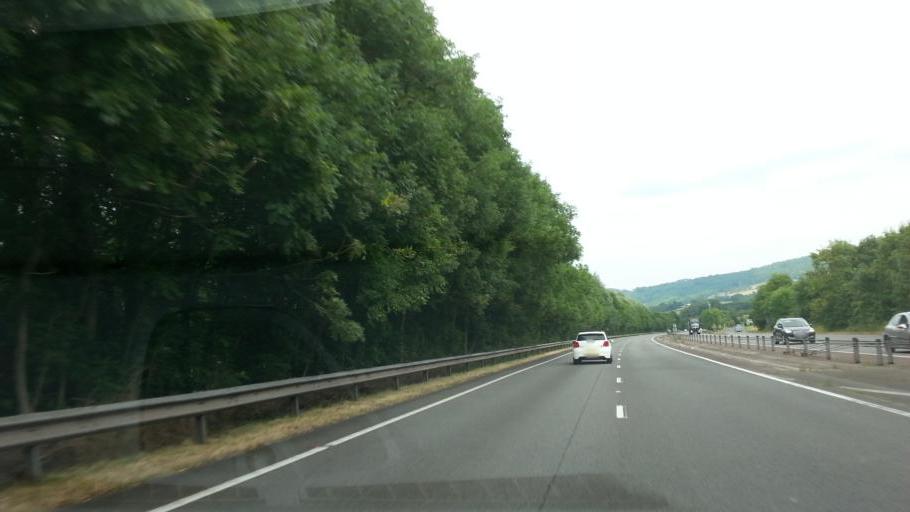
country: GB
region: Wales
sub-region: Monmouthshire
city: Mitchel Troy
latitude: 51.7898
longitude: -2.7554
